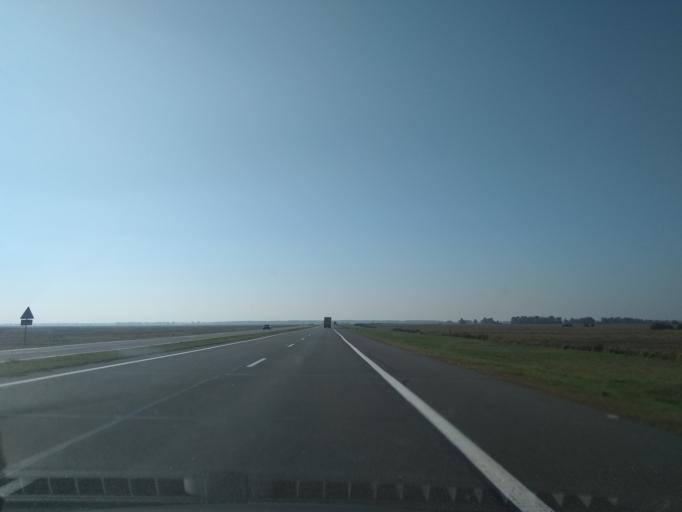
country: BY
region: Brest
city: Ivatsevichy
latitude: 52.7461
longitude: 25.4912
